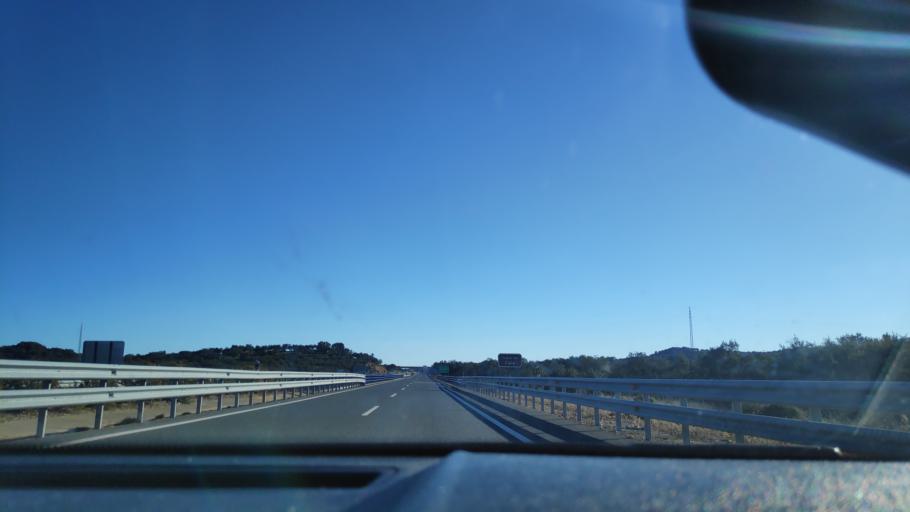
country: ES
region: Andalusia
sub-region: Provincia de Huelva
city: Santa Olalla del Cala
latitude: 37.9595
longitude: -6.2334
